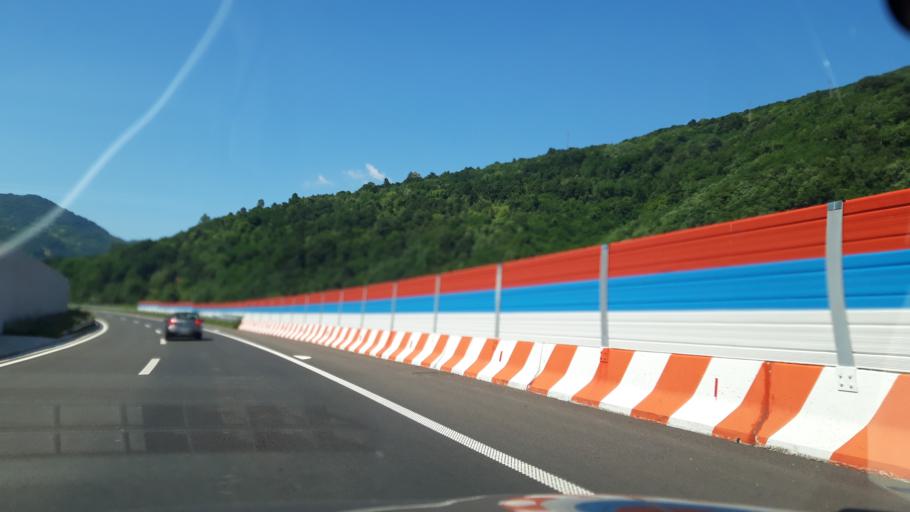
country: RS
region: Central Serbia
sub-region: Pcinjski Okrug
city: Vladicin Han
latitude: 42.7792
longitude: 22.0917
